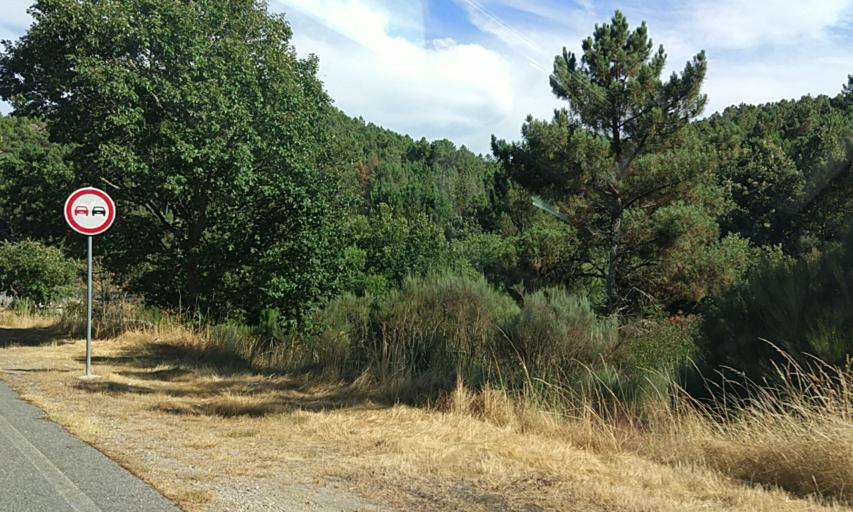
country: PT
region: Vila Real
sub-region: Sabrosa
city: Sabrosa
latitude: 41.3563
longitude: -7.5775
